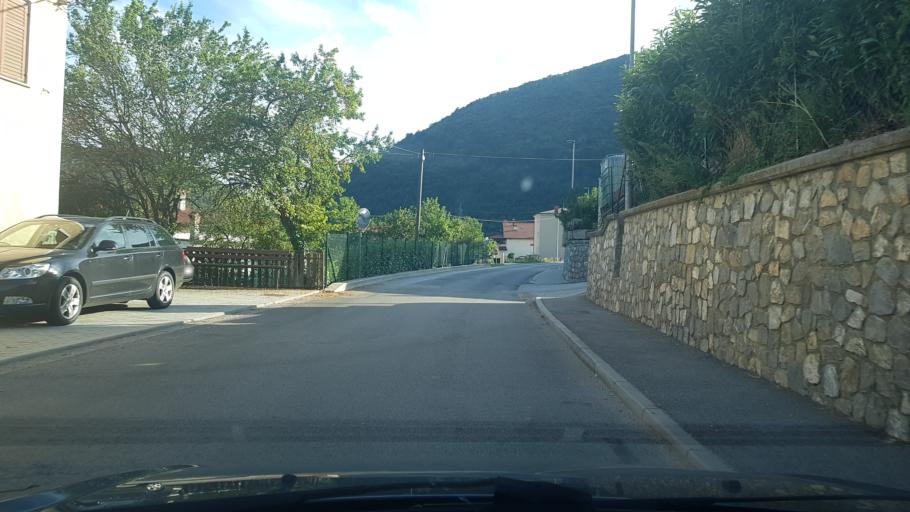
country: SI
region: Nova Gorica
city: Solkan
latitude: 46.0024
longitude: 13.6728
